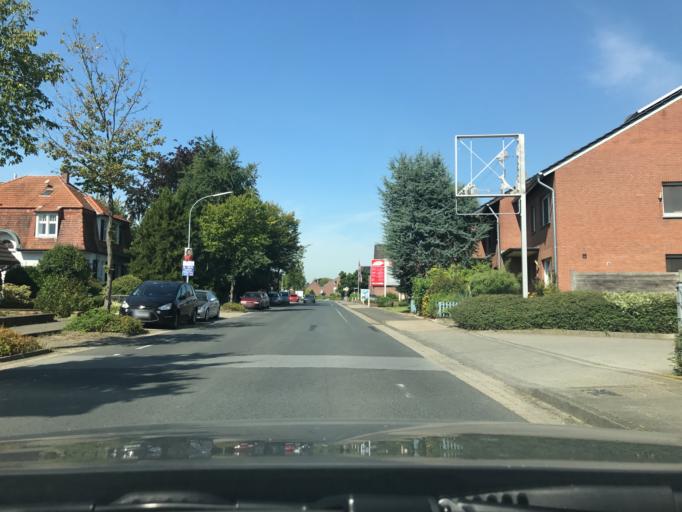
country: DE
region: North Rhine-Westphalia
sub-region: Regierungsbezirk Dusseldorf
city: Wachtendonk
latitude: 51.4073
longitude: 6.3455
